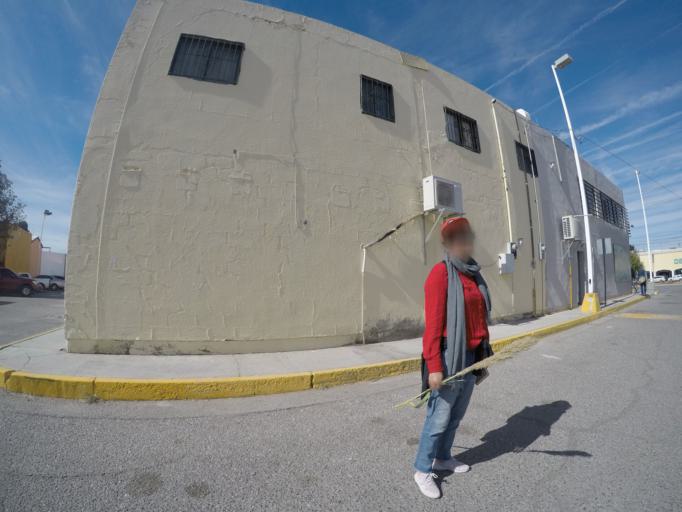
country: MX
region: Chihuahua
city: Ciudad Juarez
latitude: 31.7333
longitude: -106.4467
